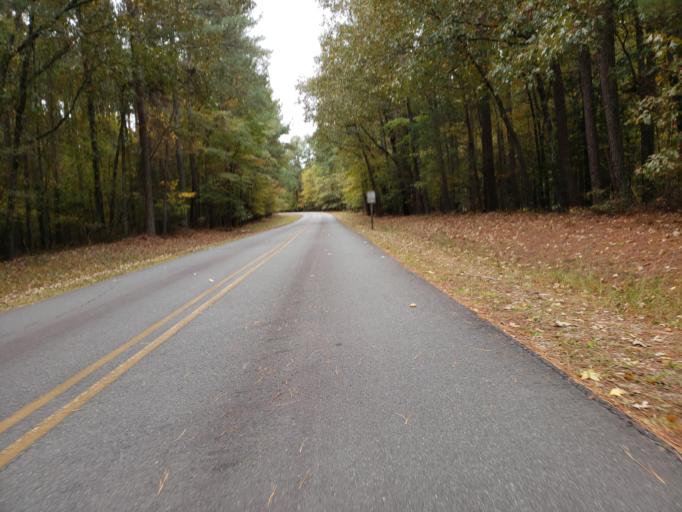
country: US
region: North Carolina
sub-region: Chatham County
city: Fearrington Village
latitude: 35.7620
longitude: -79.0444
